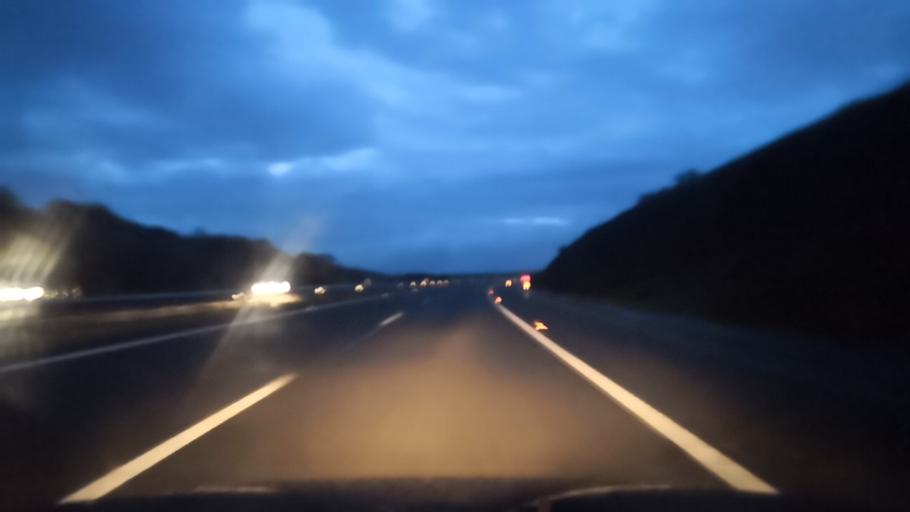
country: ES
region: Extremadura
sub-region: Provincia de Caceres
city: Caceres
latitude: 39.4066
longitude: -6.3996
